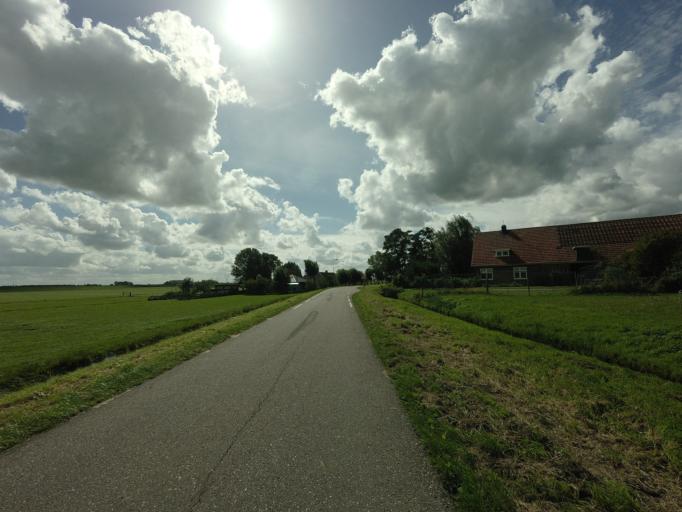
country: NL
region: North Holland
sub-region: Gemeente Waterland
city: Broek in Waterland
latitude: 52.4655
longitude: 4.9725
